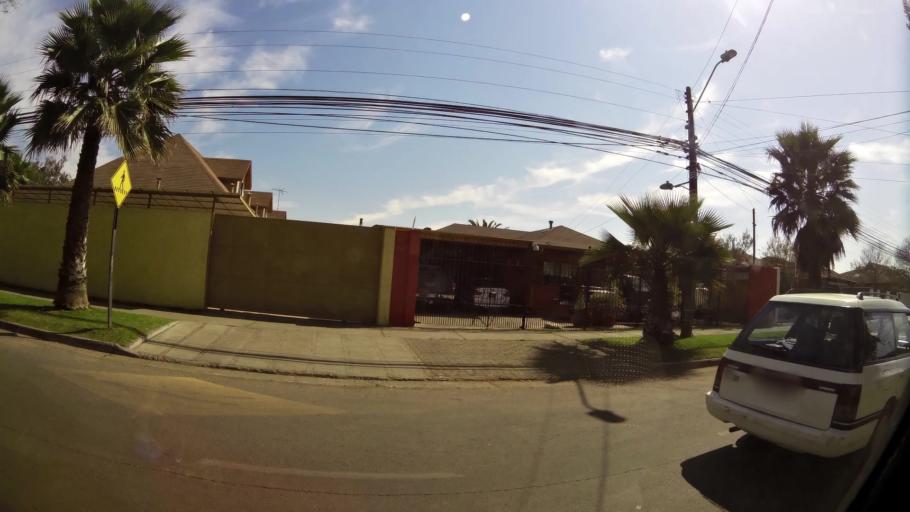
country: CL
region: Santiago Metropolitan
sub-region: Provincia de Talagante
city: Talagante
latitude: -33.6665
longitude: -70.9272
